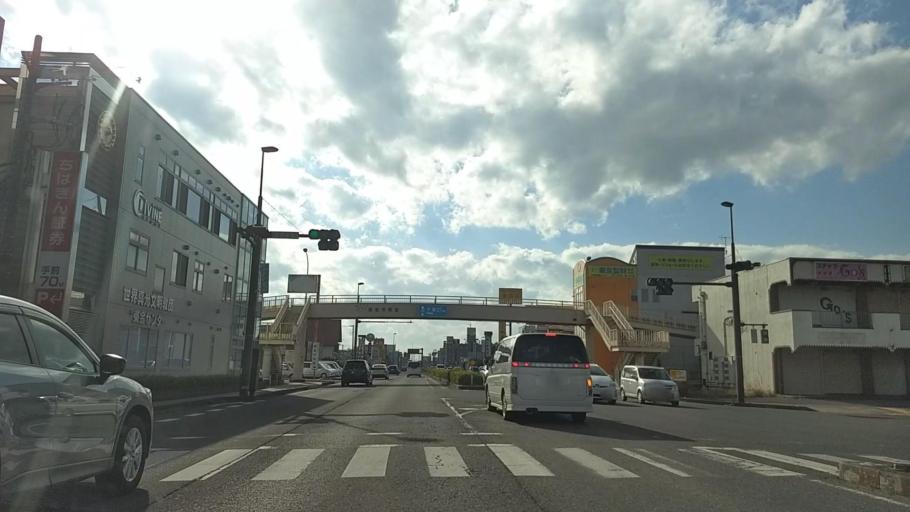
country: JP
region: Chiba
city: Togane
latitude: 35.5569
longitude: 140.3688
